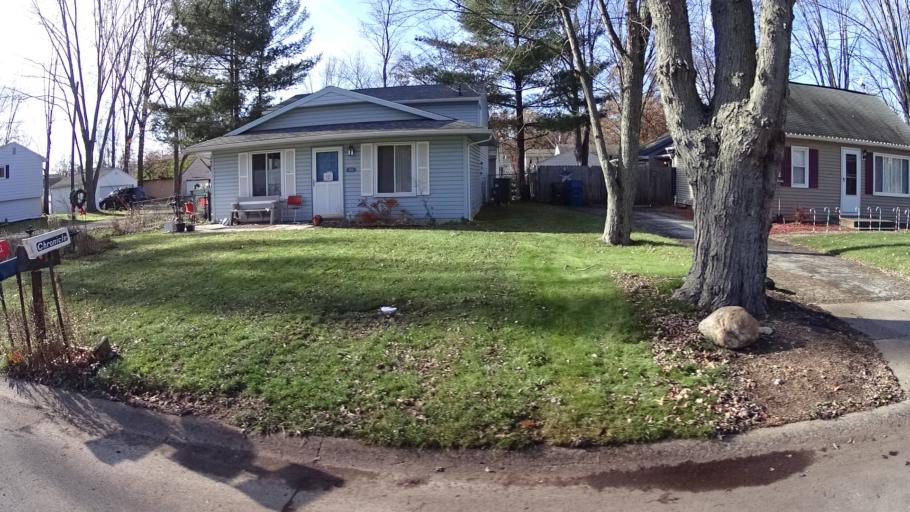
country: US
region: Ohio
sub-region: Lorain County
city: North Ridgeville
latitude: 41.4099
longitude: -81.9858
